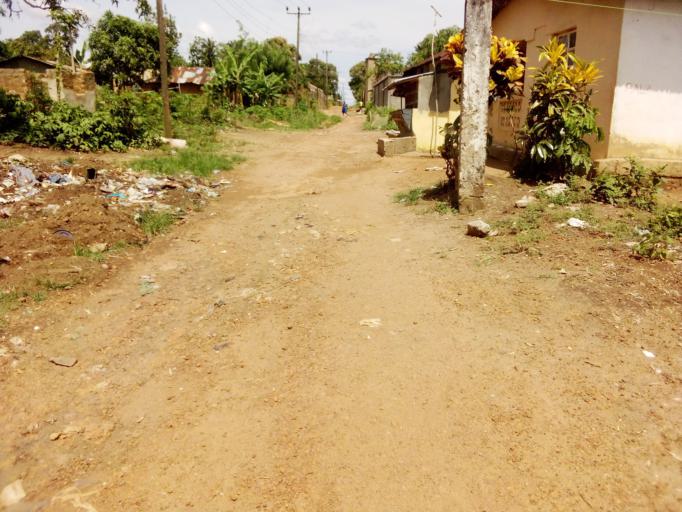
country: SL
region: Western Area
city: Waterloo
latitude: 8.3409
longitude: -13.0726
